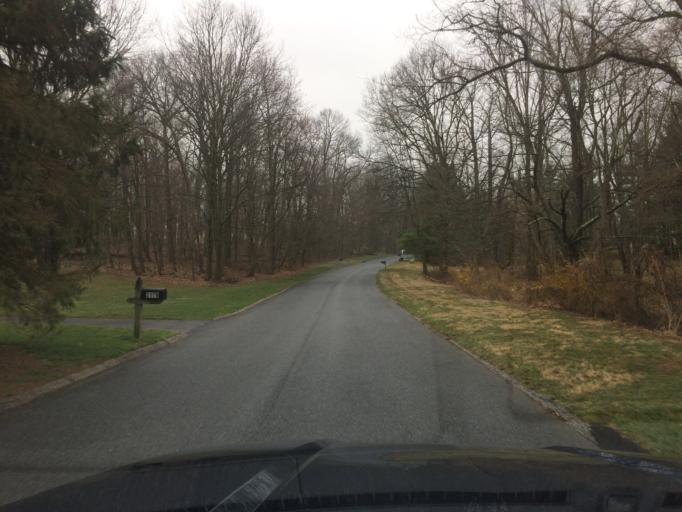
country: US
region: Maryland
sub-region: Carroll County
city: Sykesville
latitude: 39.2930
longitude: -77.0018
